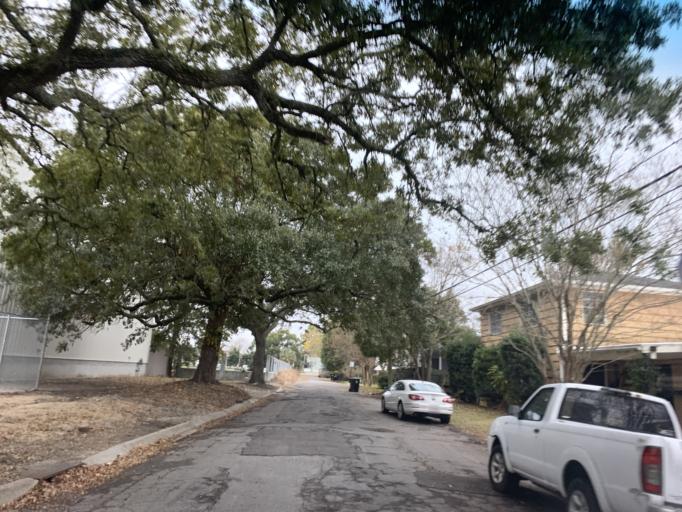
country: US
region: Louisiana
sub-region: Orleans Parish
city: New Orleans
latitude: 29.9861
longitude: -90.1073
